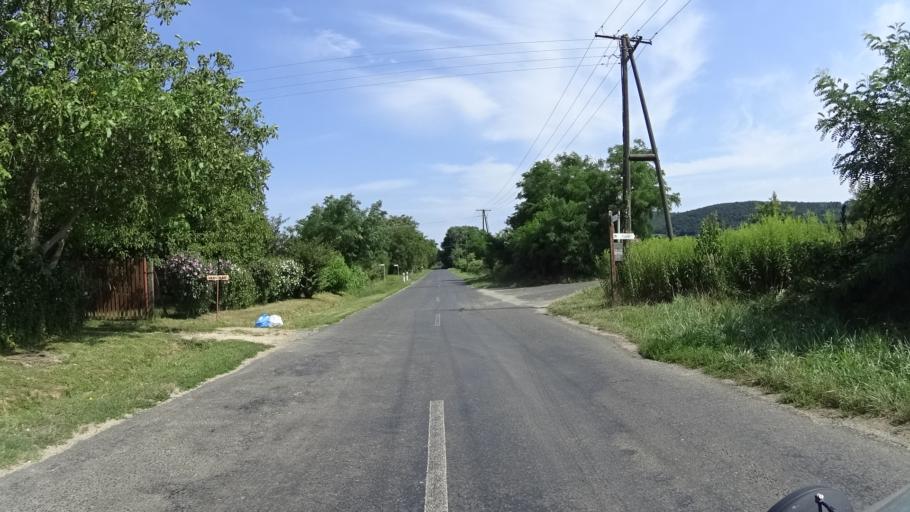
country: HU
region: Veszprem
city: Badacsonytomaj
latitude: 46.8196
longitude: 17.5148
